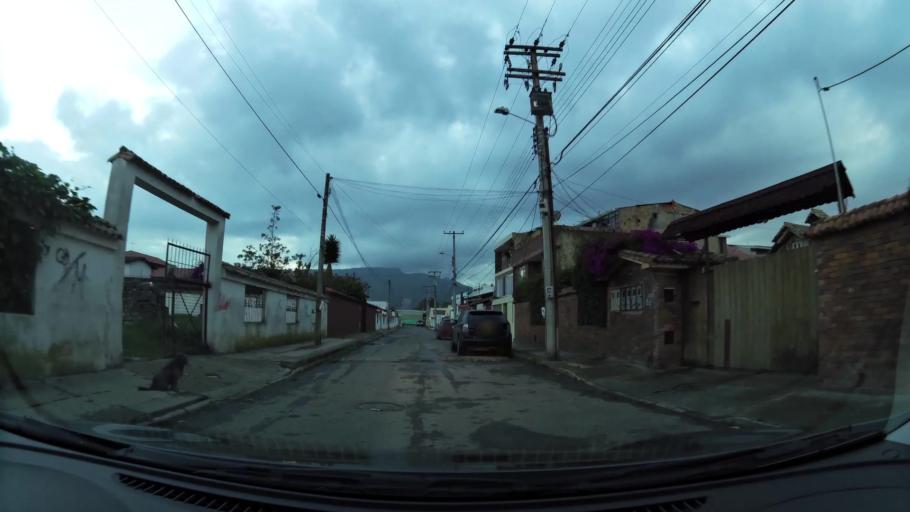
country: CO
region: Cundinamarca
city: Chia
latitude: 4.8465
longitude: -74.0576
